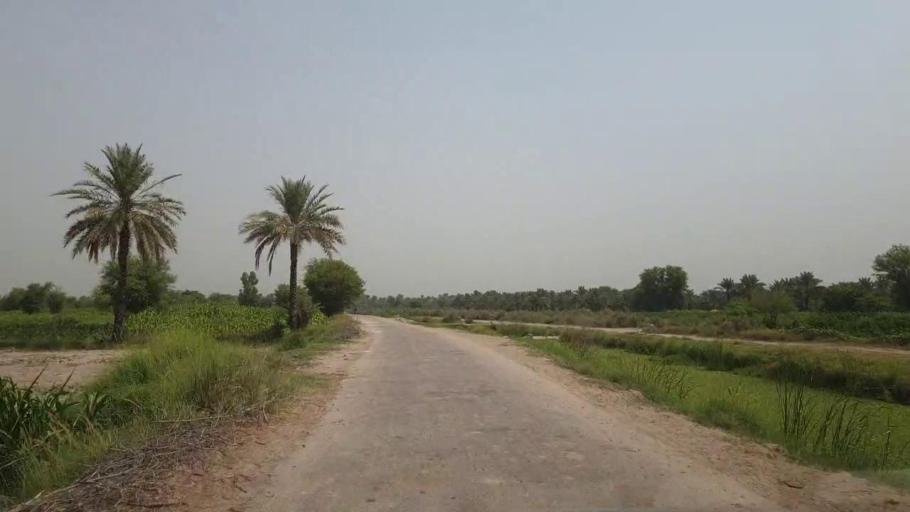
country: PK
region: Sindh
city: Gambat
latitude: 27.4310
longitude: 68.5608
